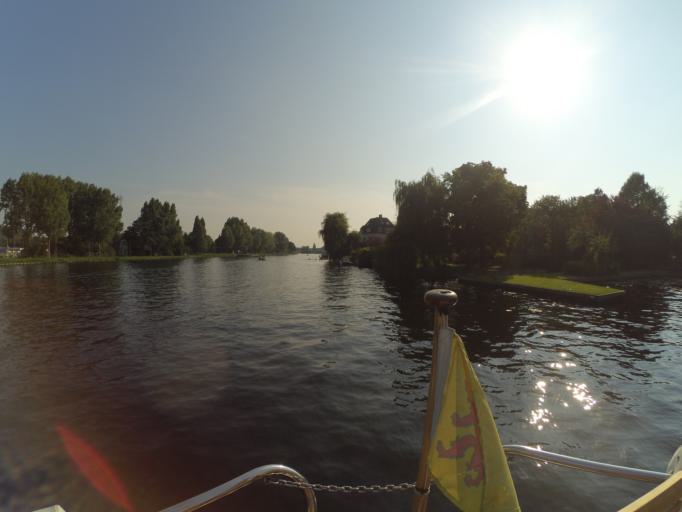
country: NL
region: North Holland
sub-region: Gemeente Haarlem
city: Haarlem
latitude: 52.3662
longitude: 4.6365
